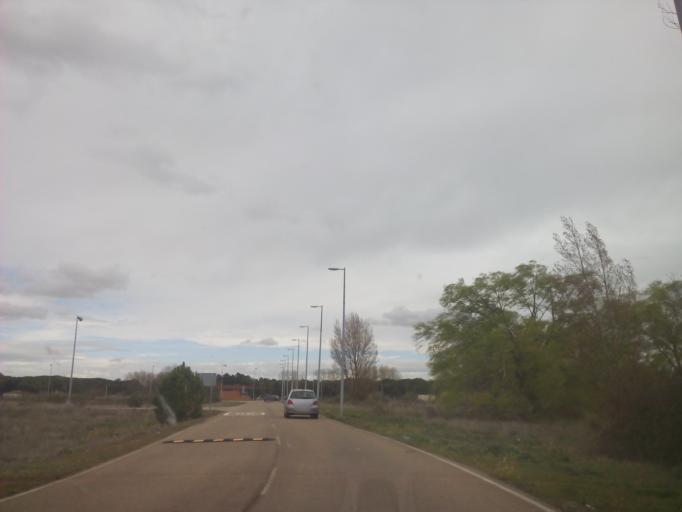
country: ES
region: Castille and Leon
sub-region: Provincia de Salamanca
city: Encinas de Abajo
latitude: 40.9401
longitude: -5.4986
